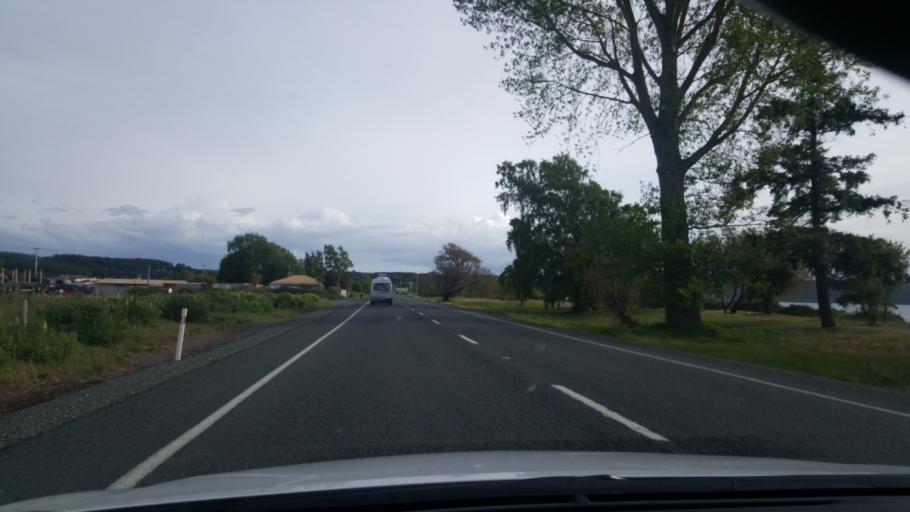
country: NZ
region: Waikato
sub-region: Taupo District
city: Taupo
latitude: -38.7756
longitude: 176.0766
